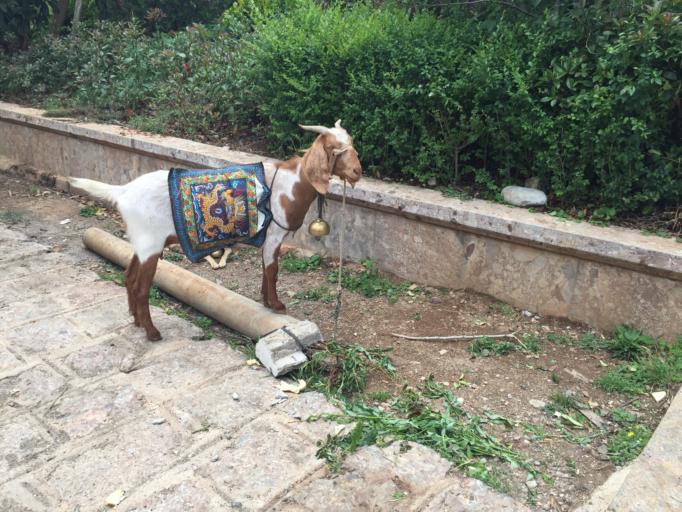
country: CN
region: Yunnan
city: Lijiang
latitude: 26.9576
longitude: 100.2170
